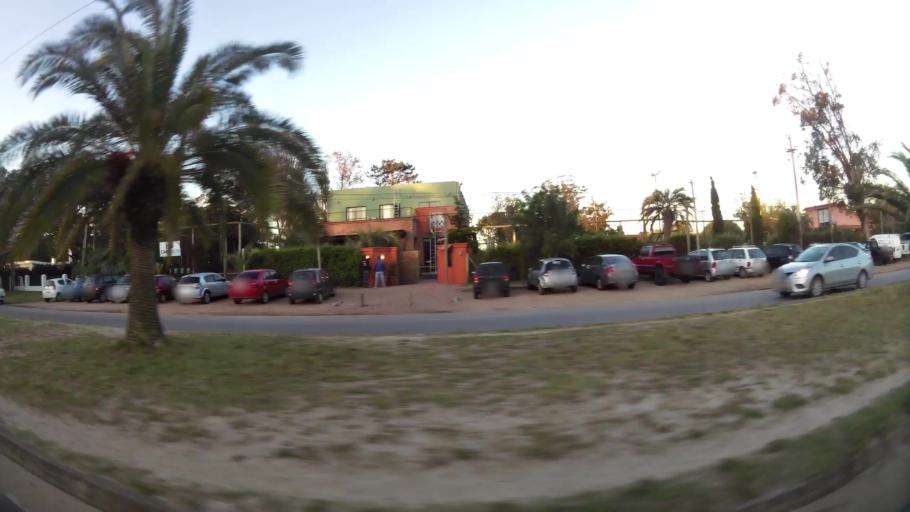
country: UY
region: Canelones
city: Barra de Carrasco
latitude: -34.8471
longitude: -55.9848
